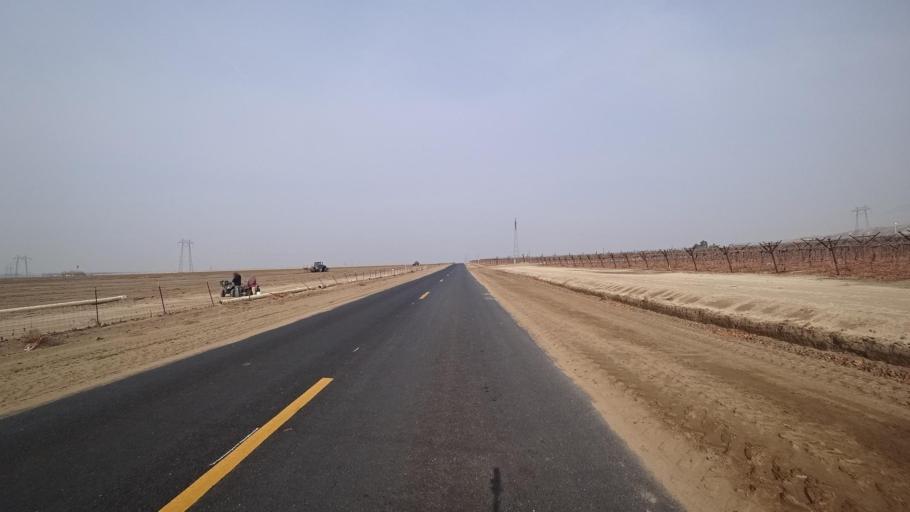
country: US
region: California
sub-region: Kern County
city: Arvin
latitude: 35.1172
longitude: -118.8506
